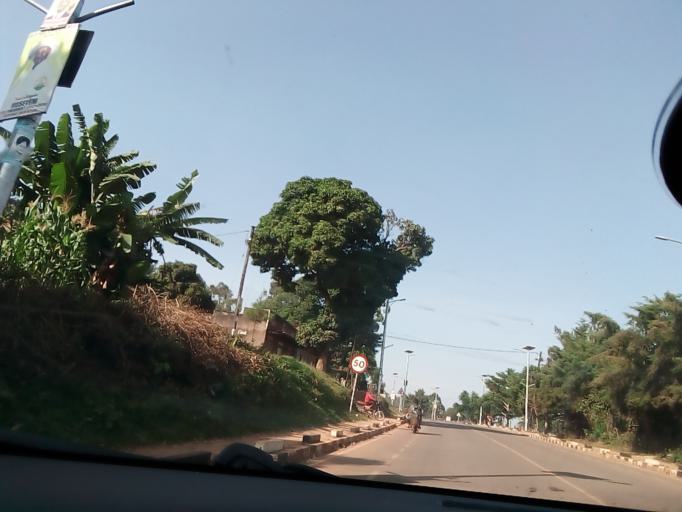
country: UG
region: Central Region
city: Masaka
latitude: -0.3230
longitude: 31.7386
